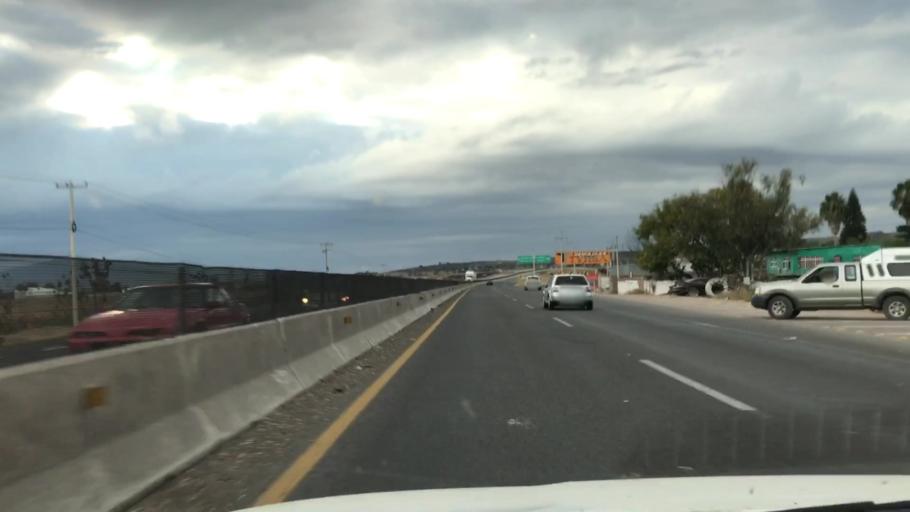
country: MX
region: Guanajuato
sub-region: Penjamo
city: Estacion la Piedad
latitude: 20.3881
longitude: -101.9461
